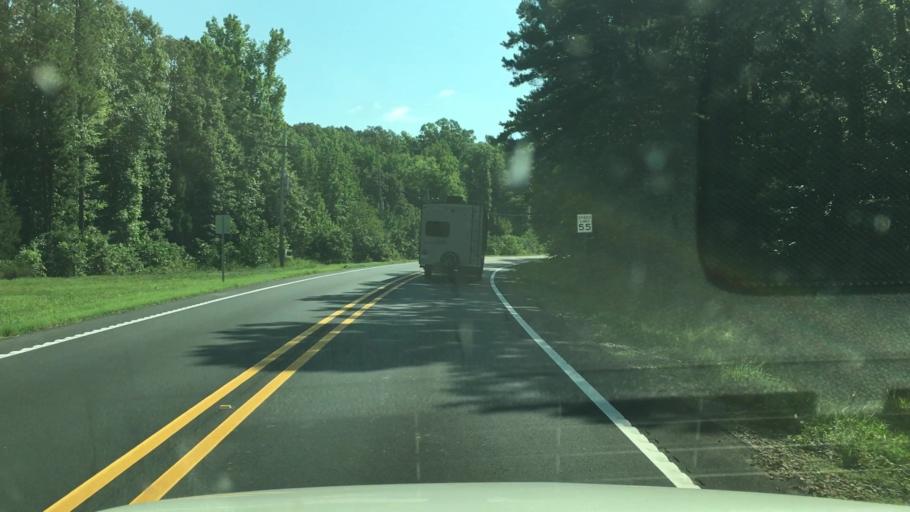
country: US
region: Arkansas
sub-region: Garland County
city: Rockwell
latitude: 34.5230
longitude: -93.3326
